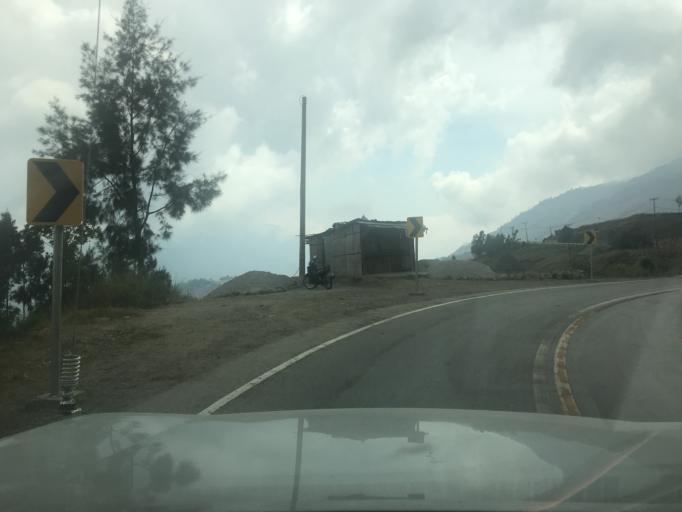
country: TL
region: Manufahi
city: Same
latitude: -8.8905
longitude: 125.5984
